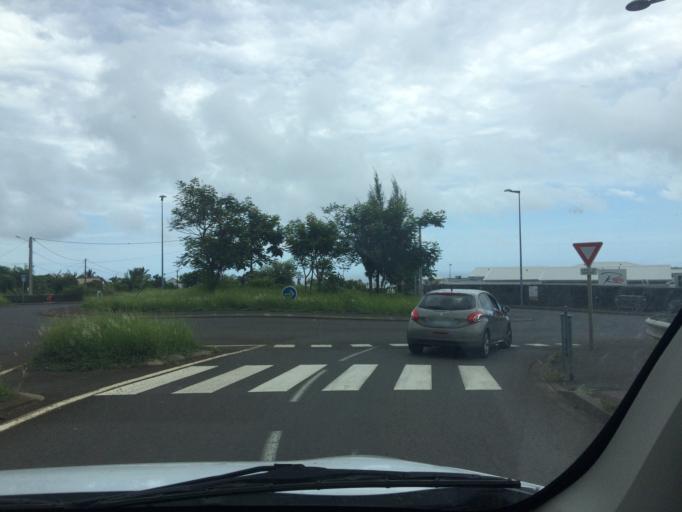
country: RE
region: Reunion
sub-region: Reunion
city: Saint-Pierre
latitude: -21.3362
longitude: 55.4878
